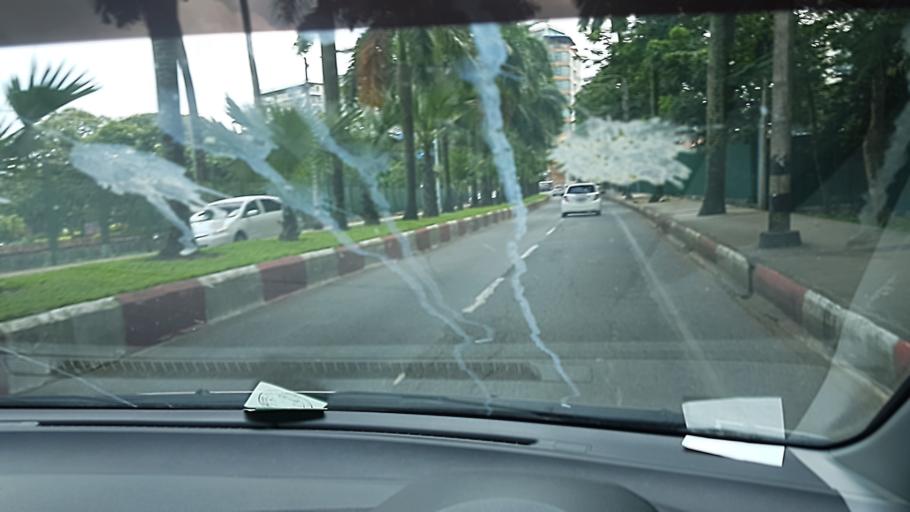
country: MM
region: Yangon
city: Yangon
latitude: 16.7926
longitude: 96.1689
